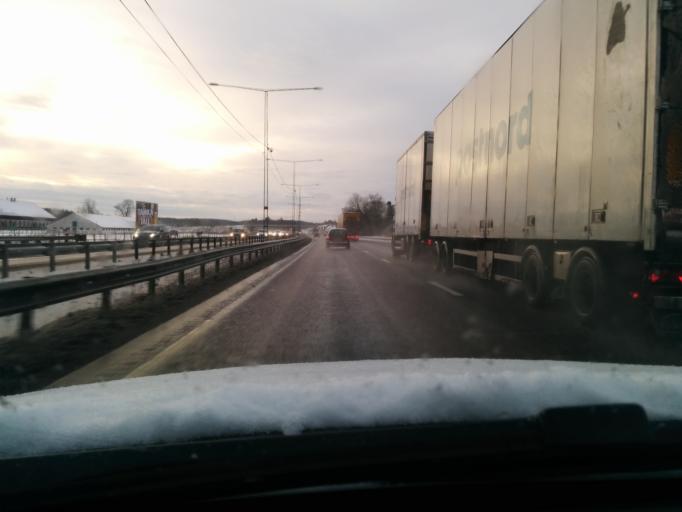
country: SE
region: Stockholm
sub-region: Sigtuna Kommun
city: Rosersberg
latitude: 59.5714
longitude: 17.8983
